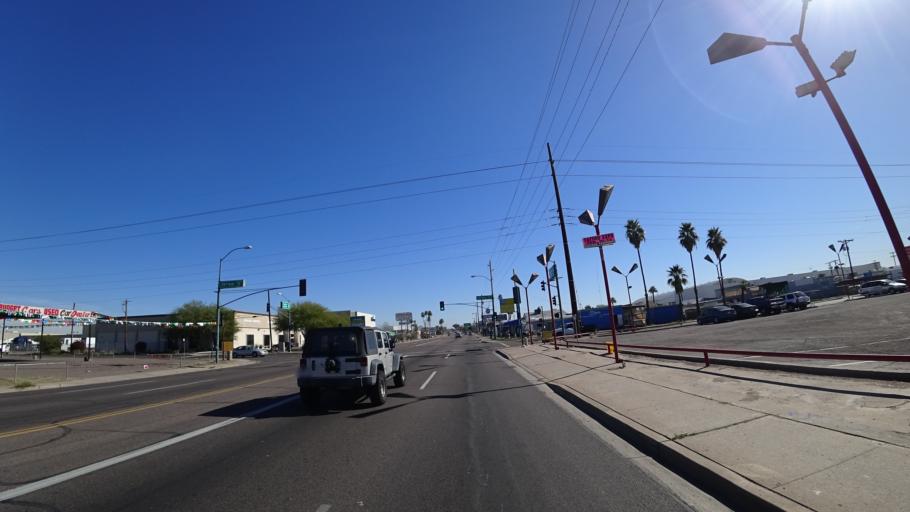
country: US
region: Arizona
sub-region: Maricopa County
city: Glendale
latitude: 33.4949
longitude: -112.1435
